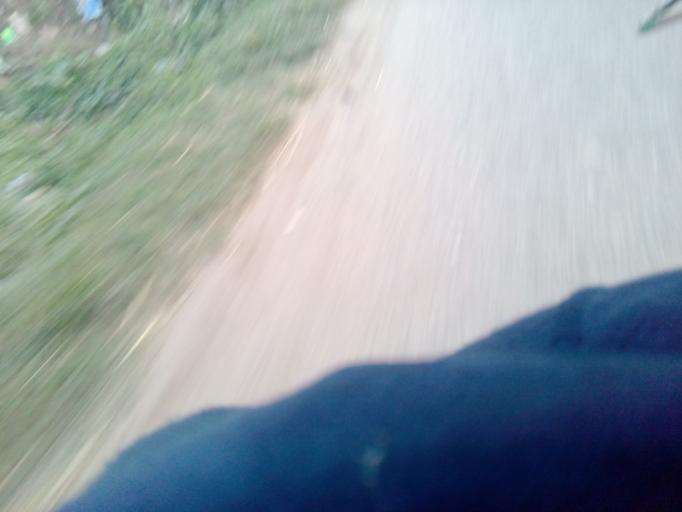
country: BD
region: Chittagong
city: Comilla
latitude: 23.4110
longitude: 91.1976
